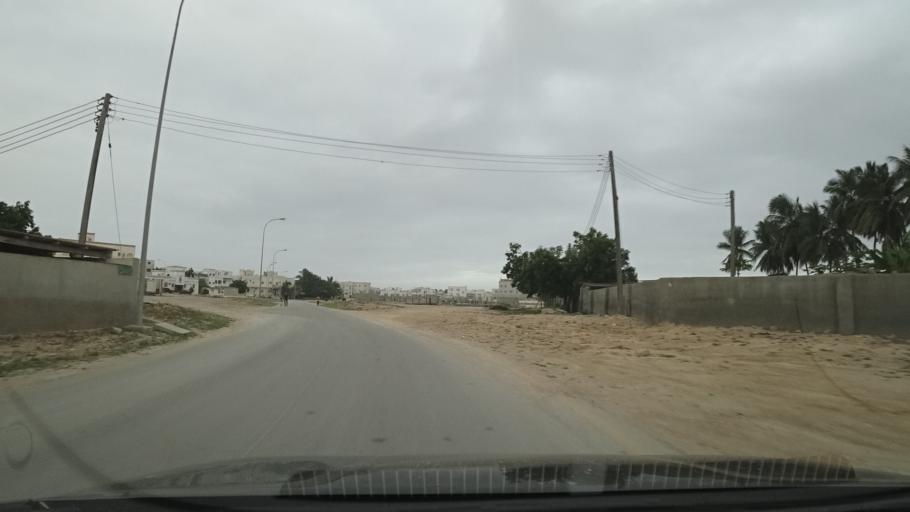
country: OM
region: Zufar
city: Salalah
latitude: 17.0243
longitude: 54.1540
